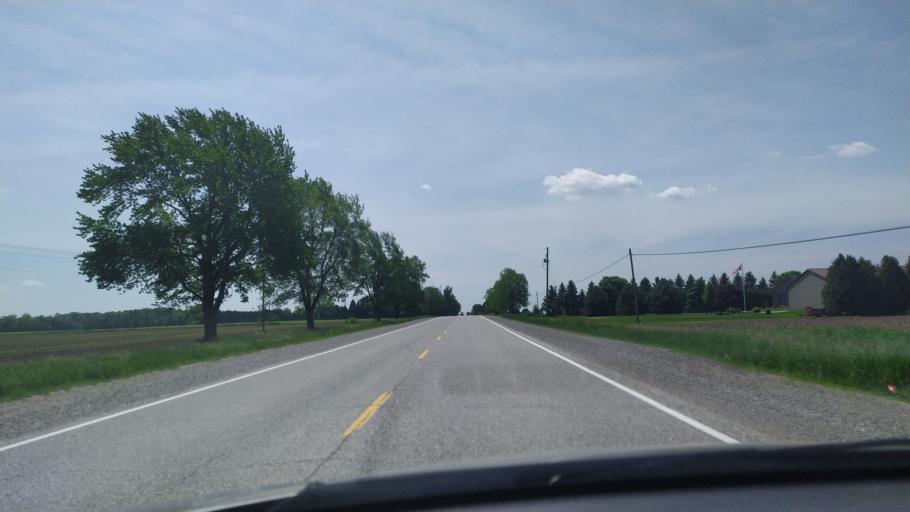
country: CA
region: Ontario
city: Dorchester
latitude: 43.1253
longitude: -81.0232
